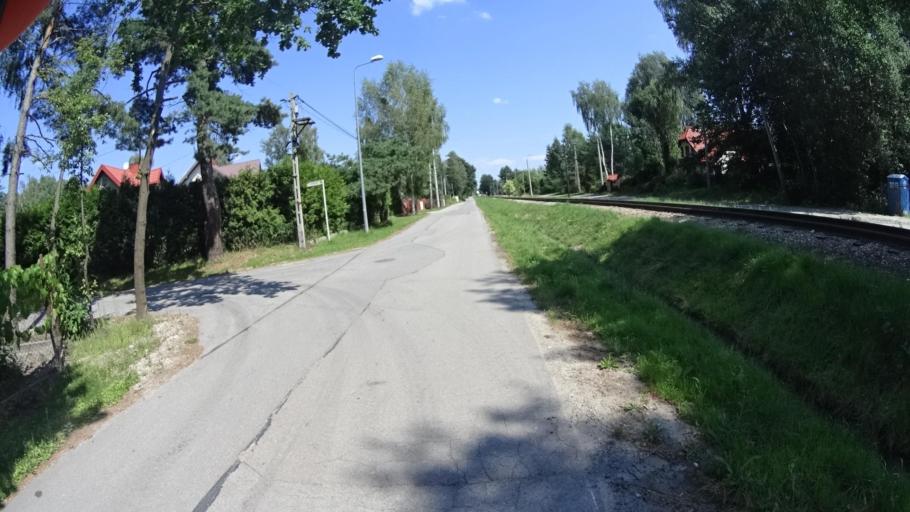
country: PL
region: Masovian Voivodeship
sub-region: Powiat piaseczynski
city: Tarczyn
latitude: 51.9991
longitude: 20.9023
